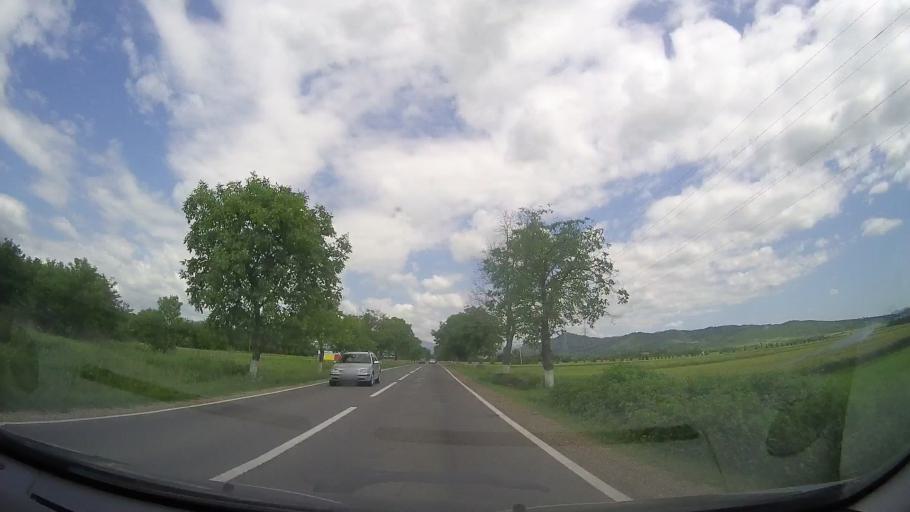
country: RO
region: Prahova
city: Drajna de Jos
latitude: 45.2305
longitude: 26.0303
